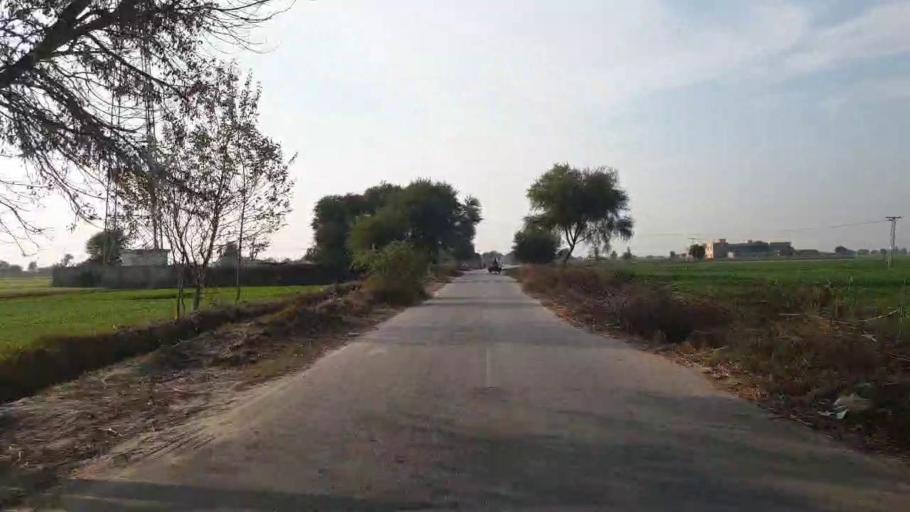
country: PK
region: Sindh
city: Shahpur Chakar
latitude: 26.1613
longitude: 68.6341
